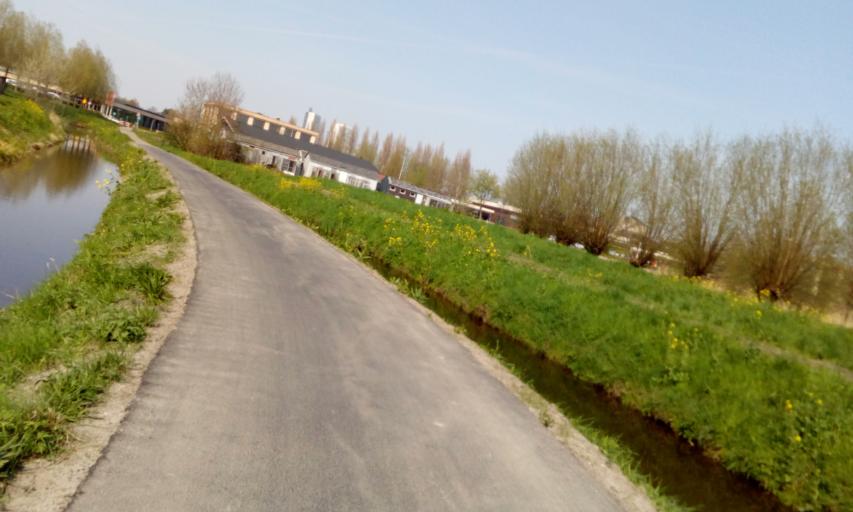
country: NL
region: South Holland
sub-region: Gemeente Spijkenisse
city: Spijkenisse
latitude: 51.8400
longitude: 4.3477
